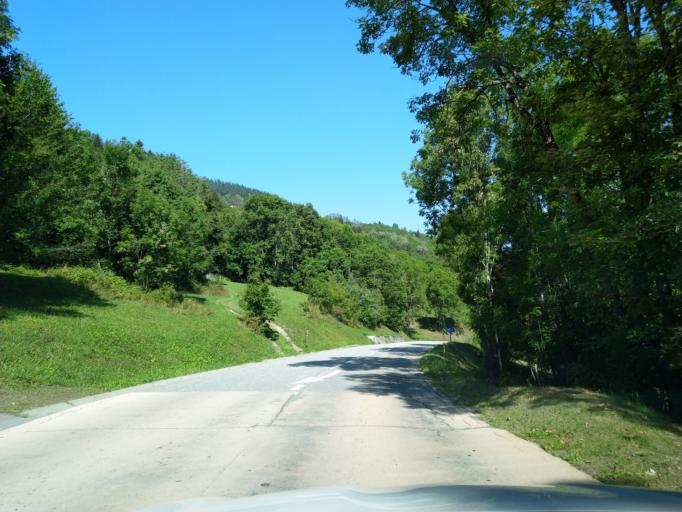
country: FR
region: Rhone-Alpes
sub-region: Departement de la Savoie
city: Les Allues
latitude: 45.4359
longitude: 6.5555
